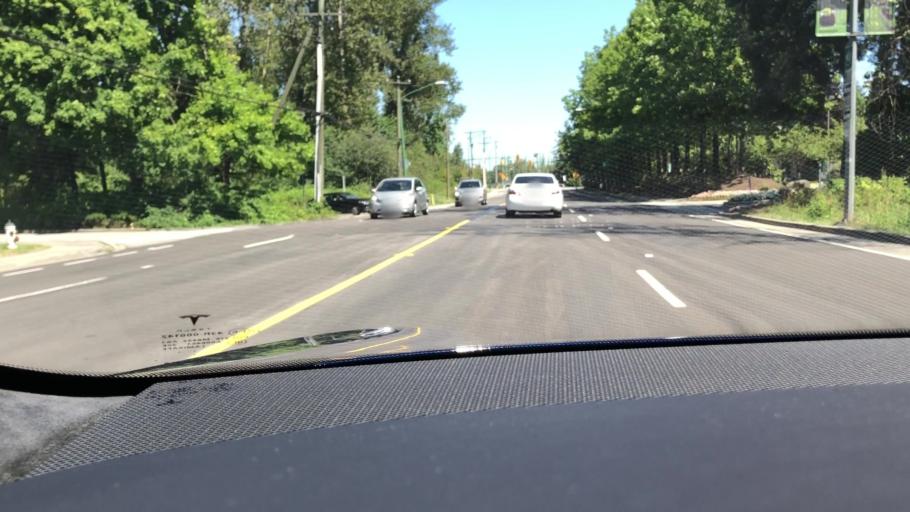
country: CA
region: British Columbia
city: Burnaby
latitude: 49.2499
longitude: -122.9695
